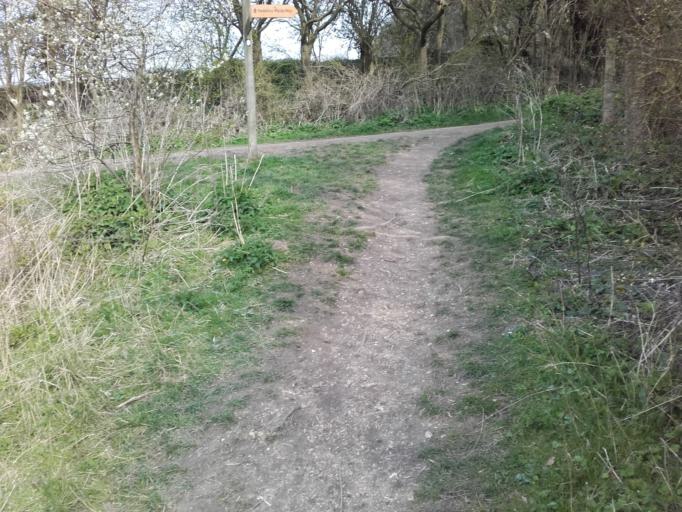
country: GB
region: England
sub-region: East Riding of Yorkshire
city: South Cave
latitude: 53.7764
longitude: -0.5914
